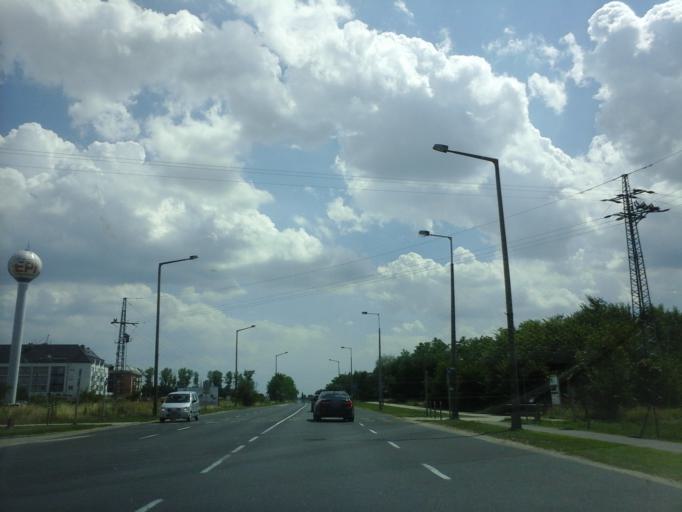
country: HU
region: Gyor-Moson-Sopron
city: Rajka
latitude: 47.9907
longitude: 17.1959
